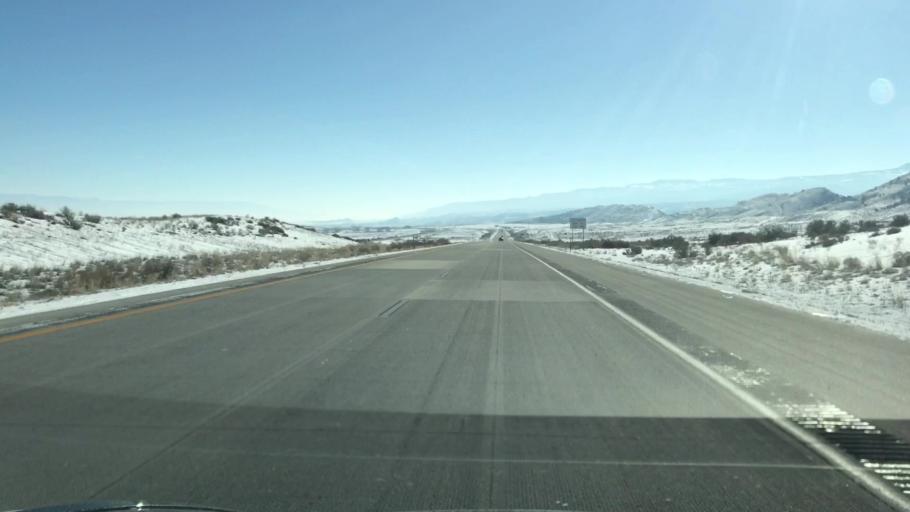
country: US
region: Colorado
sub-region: Mesa County
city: Loma
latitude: 39.1929
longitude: -108.8418
